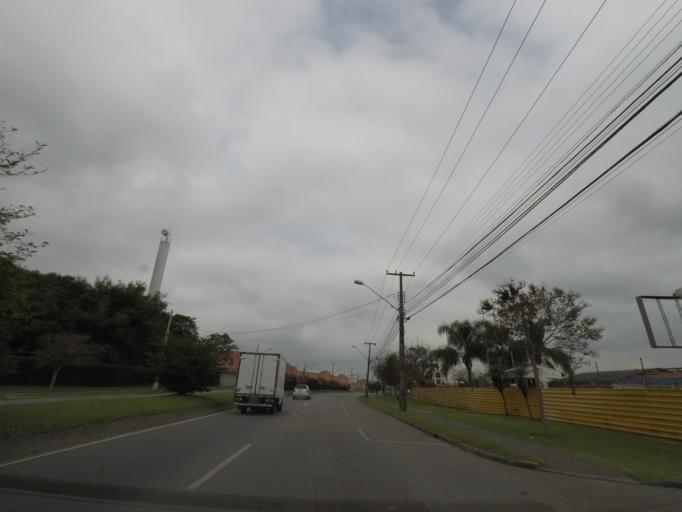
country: BR
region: Parana
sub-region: Curitiba
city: Curitiba
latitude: -25.5074
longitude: -49.3294
